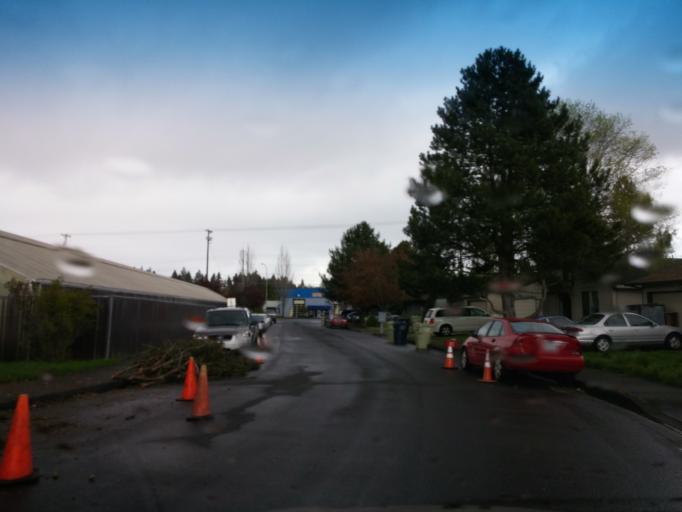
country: US
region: Oregon
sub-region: Washington County
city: Aloha
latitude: 45.5126
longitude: -122.8614
